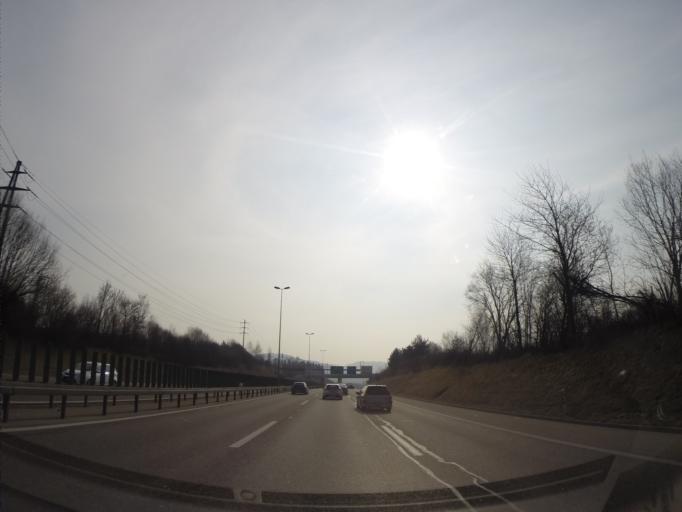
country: CH
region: Zurich
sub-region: Bezirk Winterthur
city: Wuelflingen (Kreis 6) / Lindenplatz
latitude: 47.5204
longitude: 8.6973
